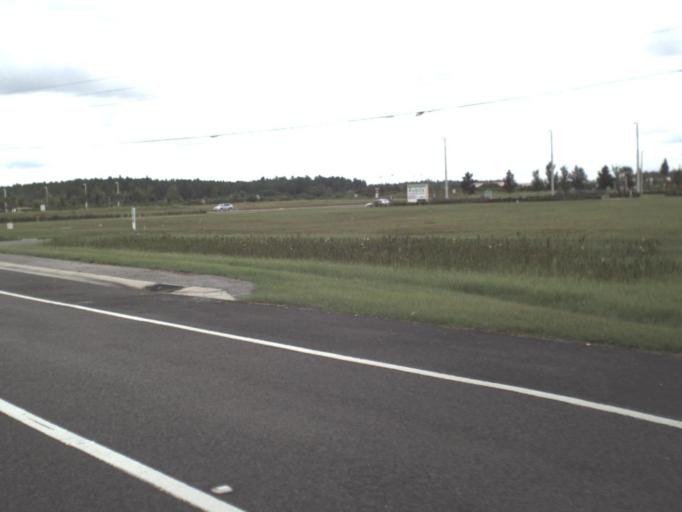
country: US
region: Florida
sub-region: Hillsborough County
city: Cheval
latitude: 28.1935
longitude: -82.5041
